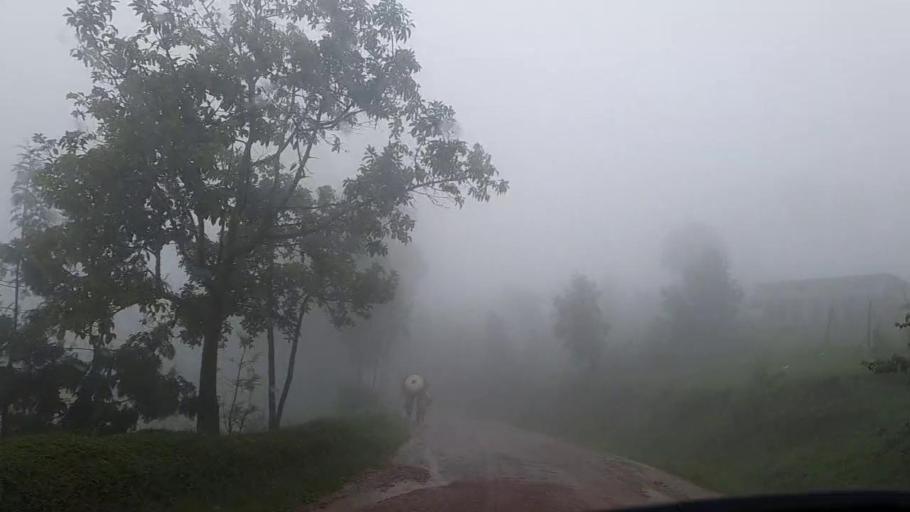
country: RW
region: Kigali
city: Kigali
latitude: -1.7692
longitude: 29.9968
